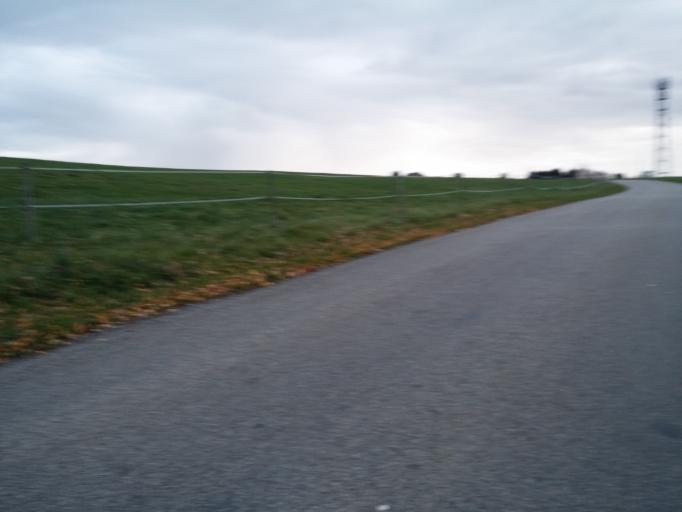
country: DE
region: Bavaria
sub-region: Upper Bavaria
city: Grafing bei Munchen
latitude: 48.0268
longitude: 11.9844
